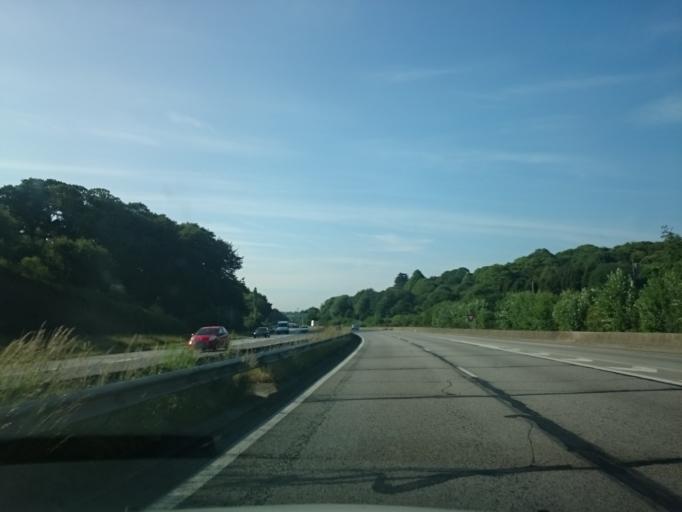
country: FR
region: Brittany
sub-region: Departement du Finistere
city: Quimper
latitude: 48.0269
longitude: -4.0862
